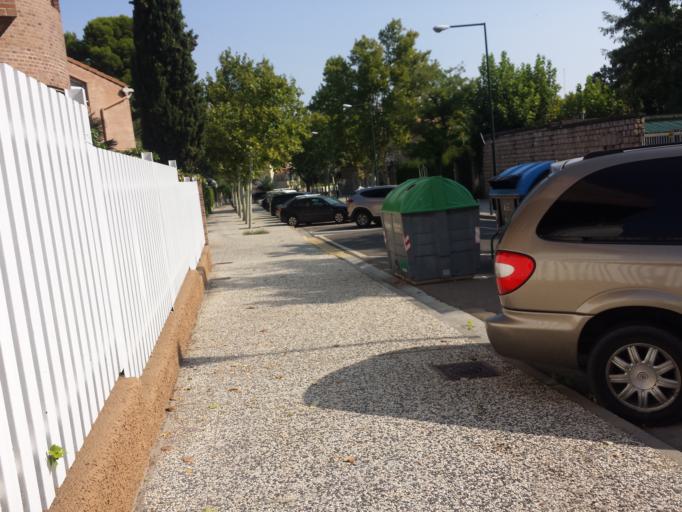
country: ES
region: Aragon
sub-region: Provincia de Zaragoza
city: Delicias
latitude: 41.6344
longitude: -0.8907
